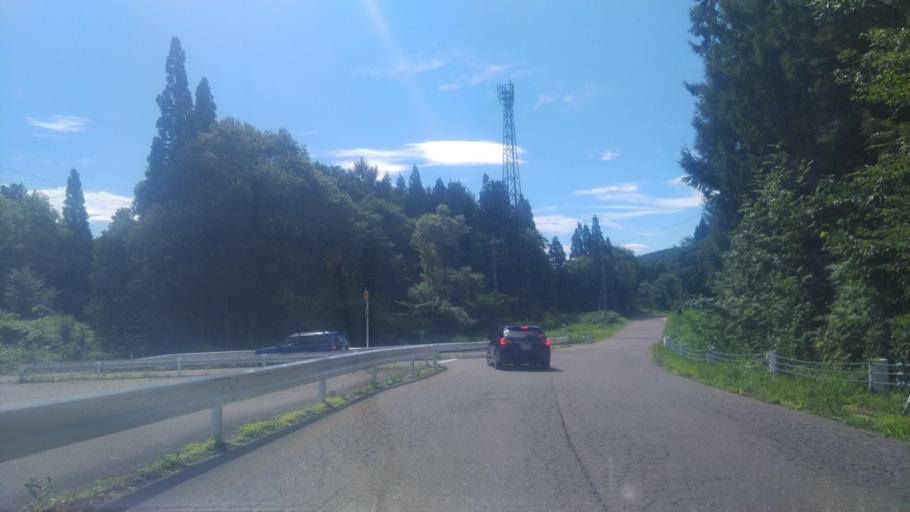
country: JP
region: Niigata
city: Arai
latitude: 36.8381
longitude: 138.1685
